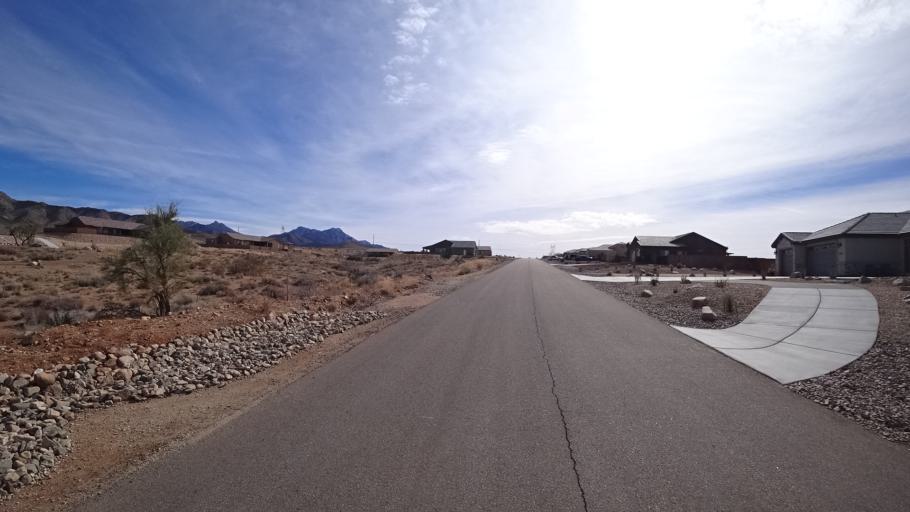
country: US
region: Arizona
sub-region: Mohave County
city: Kingman
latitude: 35.1839
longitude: -113.9780
